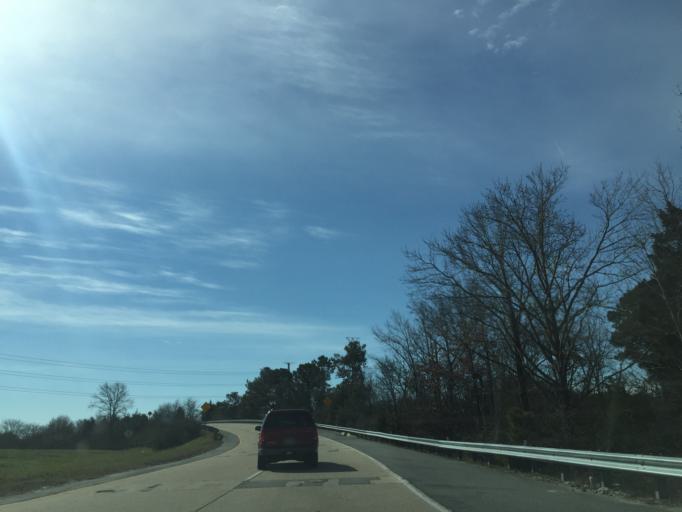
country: US
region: Virginia
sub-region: City of Norfolk
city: Norfolk
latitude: 36.9071
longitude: -76.2584
